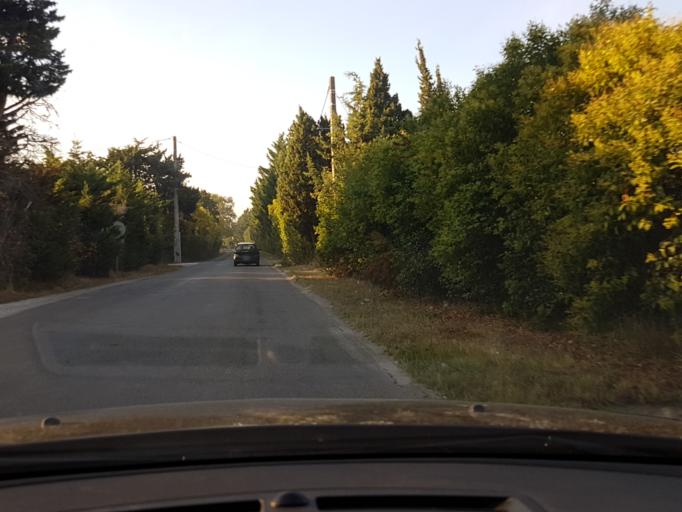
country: FR
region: Provence-Alpes-Cote d'Azur
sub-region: Departement des Bouches-du-Rhone
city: Molleges
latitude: 43.8175
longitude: 4.9481
